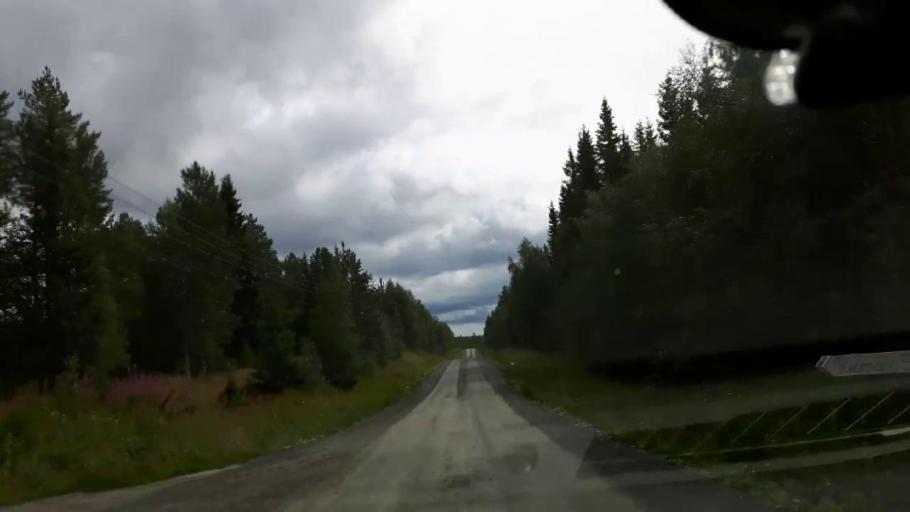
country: SE
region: Jaemtland
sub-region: Krokoms Kommun
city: Valla
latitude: 63.6088
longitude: 14.1192
